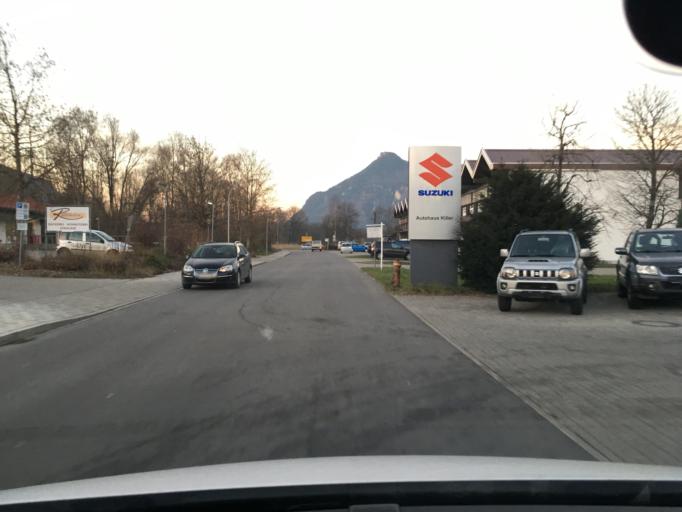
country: DE
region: Bavaria
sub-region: Upper Bavaria
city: Oberaudorf
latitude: 47.6483
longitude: 12.1790
